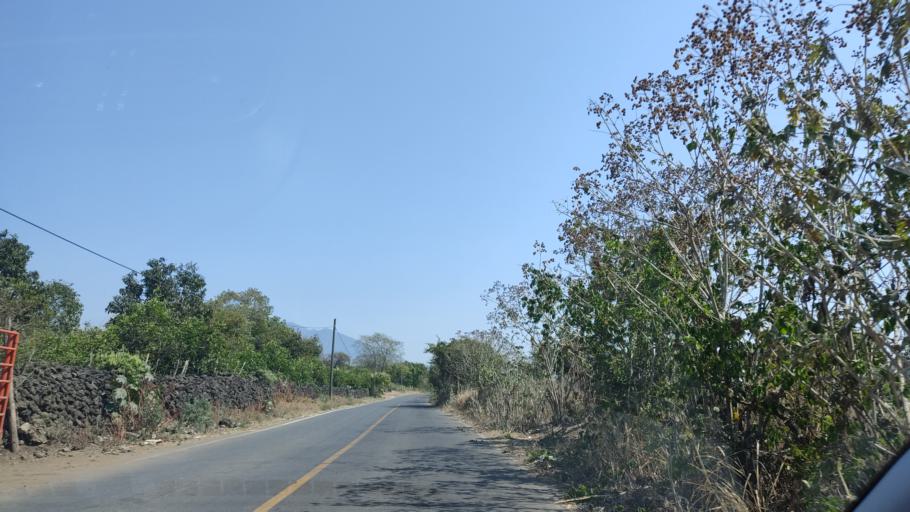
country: MX
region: Nayarit
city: Puga
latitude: 21.5348
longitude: -104.8094
